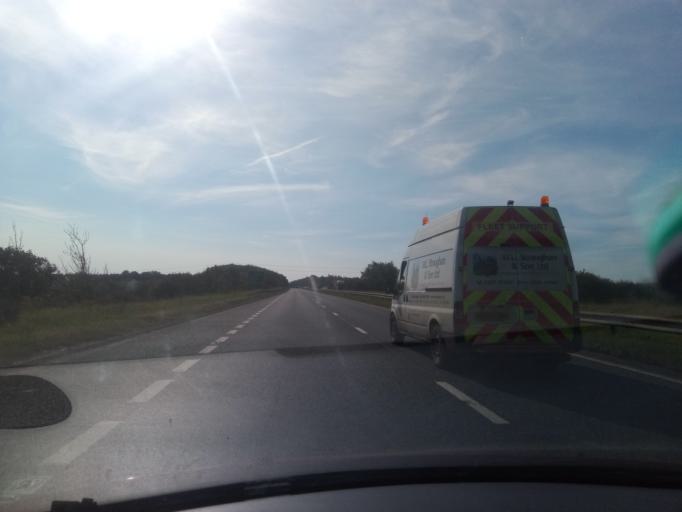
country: GB
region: England
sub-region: County Durham
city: Seaham
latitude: 54.8342
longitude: -1.3746
